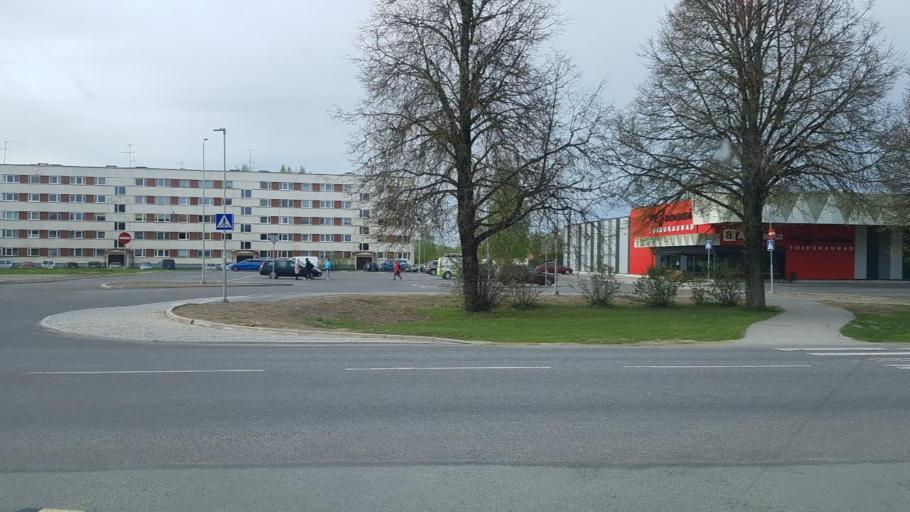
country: EE
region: Polvamaa
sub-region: Polva linn
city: Polva
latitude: 58.0528
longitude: 27.0442
